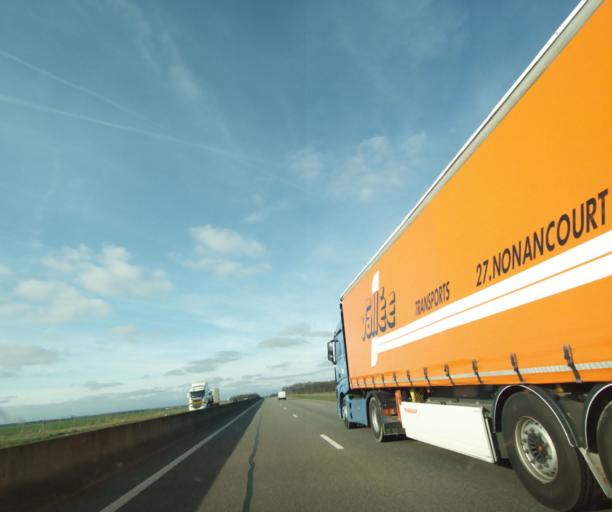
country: FR
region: Ile-de-France
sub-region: Departement des Yvelines
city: Sonchamp
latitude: 48.5966
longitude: 1.8319
